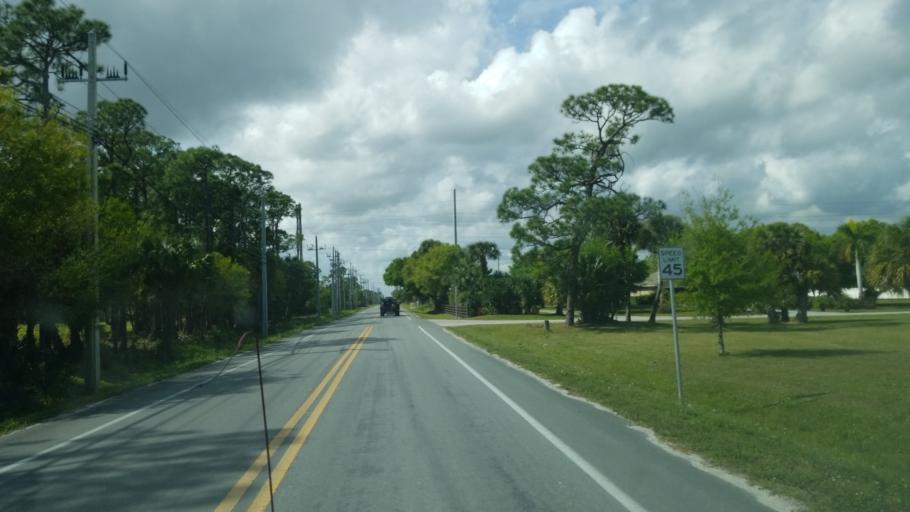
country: US
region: Florida
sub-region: Saint Lucie County
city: Lakewood Park
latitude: 27.4477
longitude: -80.4486
